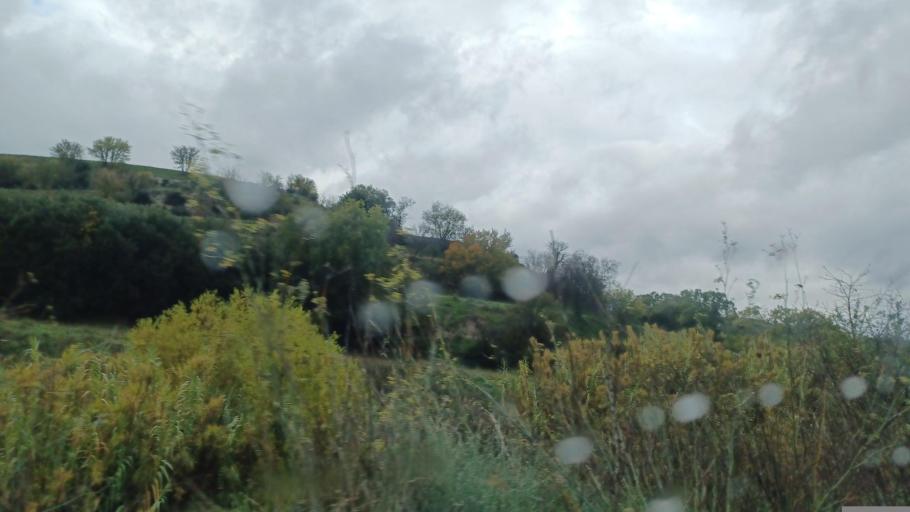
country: CY
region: Pafos
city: Mesogi
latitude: 34.8612
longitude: 32.5409
